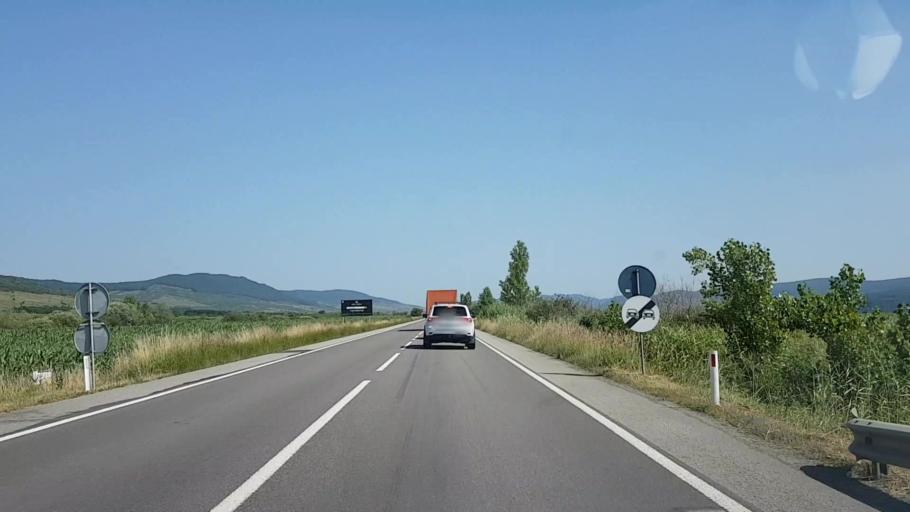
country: RO
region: Bistrita-Nasaud
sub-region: Comuna Sieu-Odorhei
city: Sieu-Odorhei
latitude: 47.1249
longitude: 24.3211
